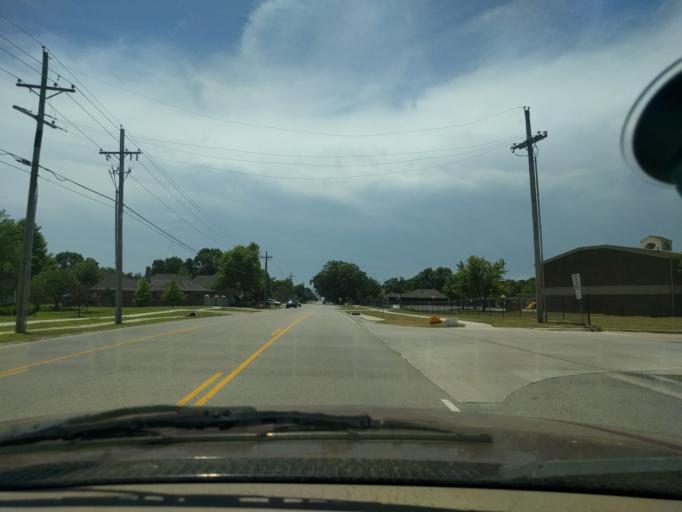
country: US
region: Oklahoma
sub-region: Tulsa County
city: Jenks
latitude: 36.0156
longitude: -95.9222
